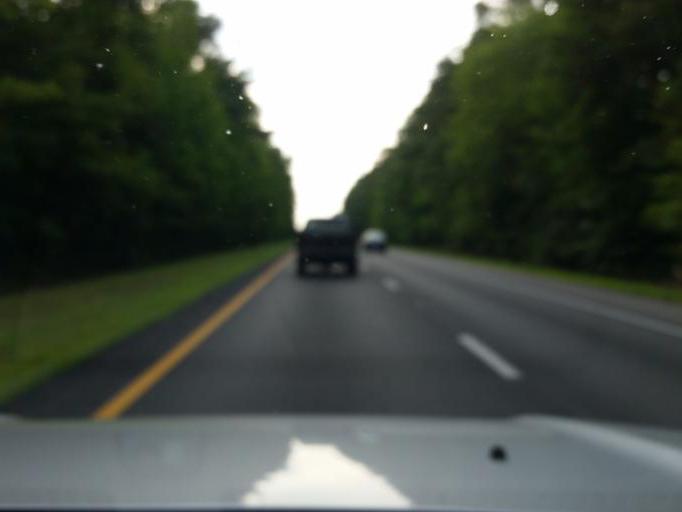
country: US
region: Virginia
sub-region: King William County
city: West Point
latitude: 37.4428
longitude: -76.8558
